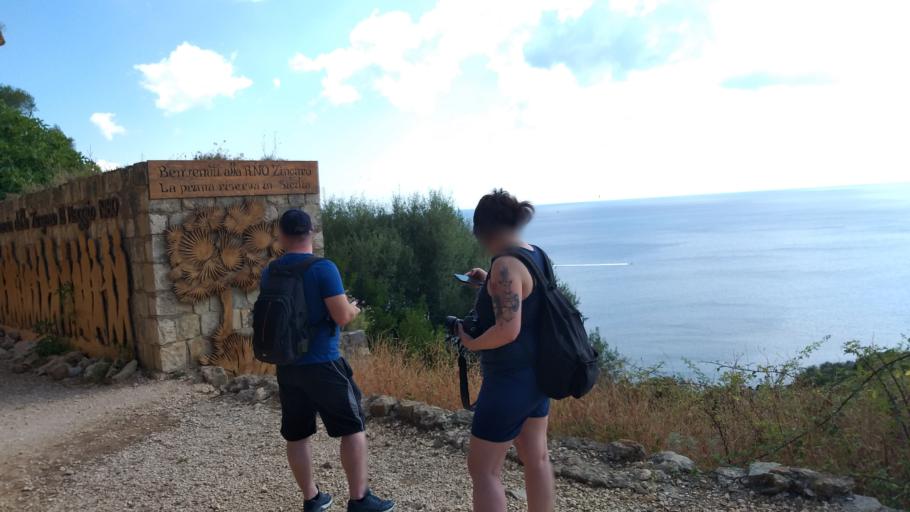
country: IT
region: Sicily
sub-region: Trapani
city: Castelluzzo
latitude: 38.0826
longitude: 12.8075
